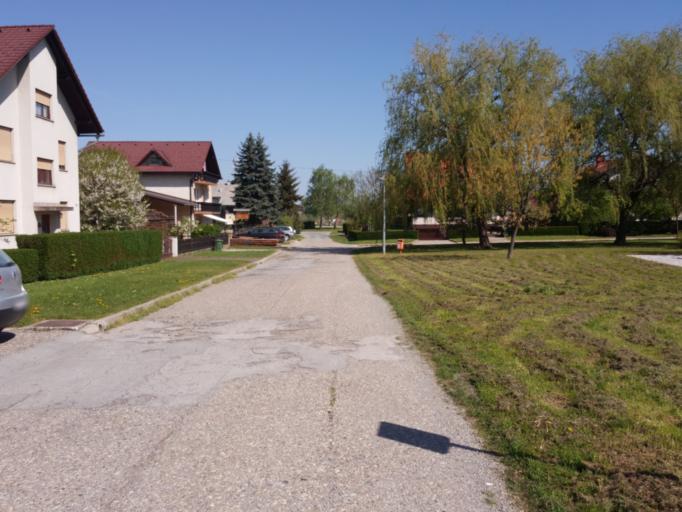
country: HR
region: Varazdinska
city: Ivanec
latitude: 46.2277
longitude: 16.1278
